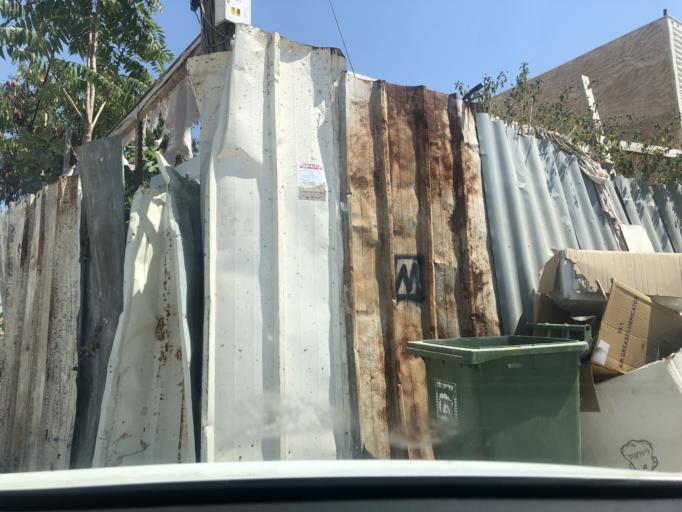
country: IL
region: Central District
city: Lod
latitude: 31.9581
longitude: 34.9004
